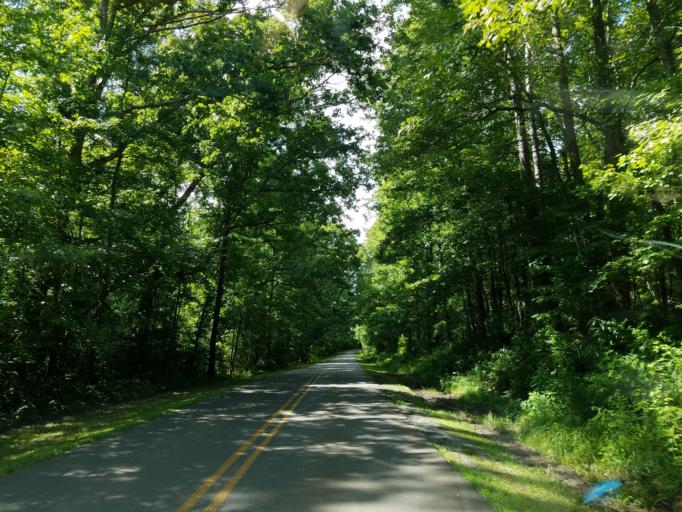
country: US
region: Georgia
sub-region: Pickens County
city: Nelson
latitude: 34.3921
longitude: -84.3752
